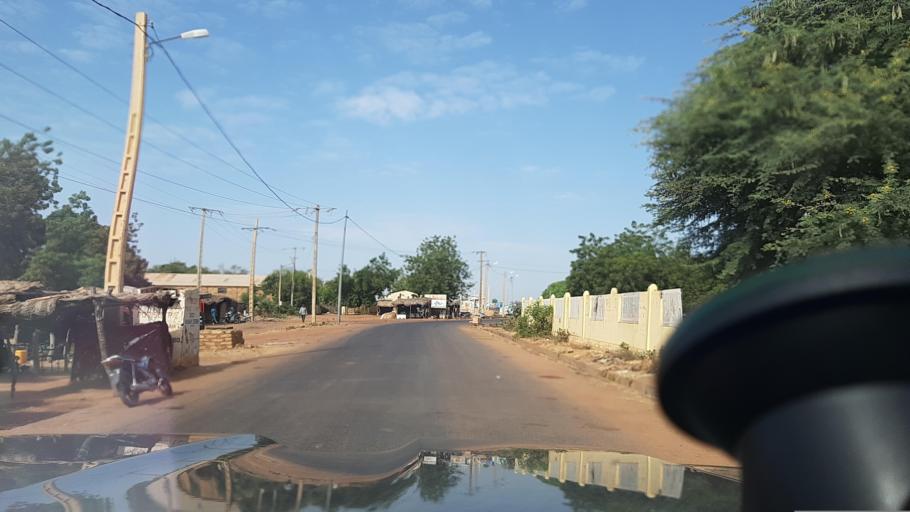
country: ML
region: Segou
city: Markala
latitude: 13.6778
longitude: -6.0749
